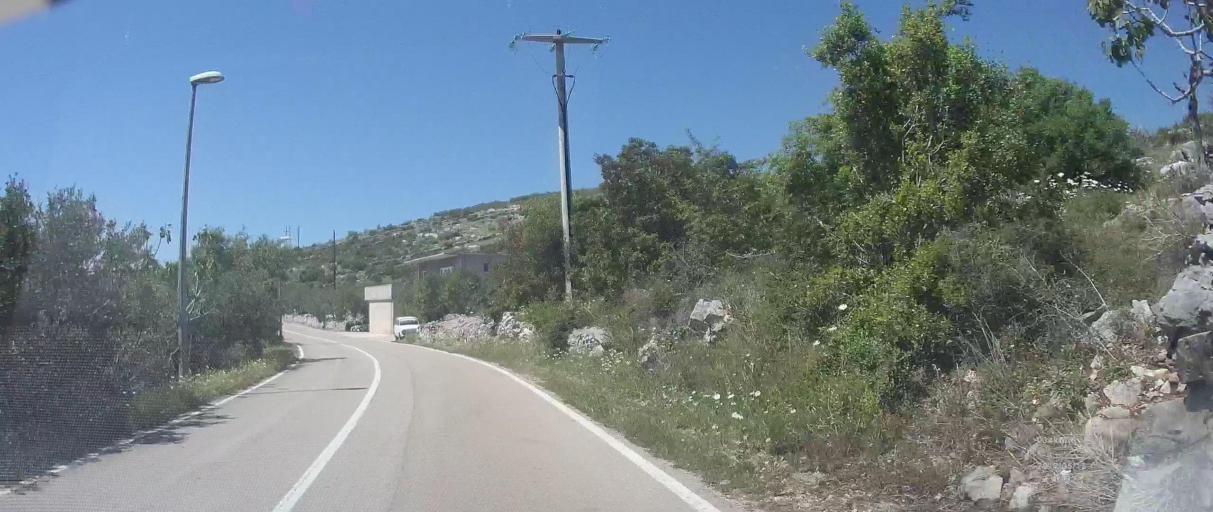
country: HR
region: Sibensko-Kniniska
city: Primosten
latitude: 43.6111
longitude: 15.9821
